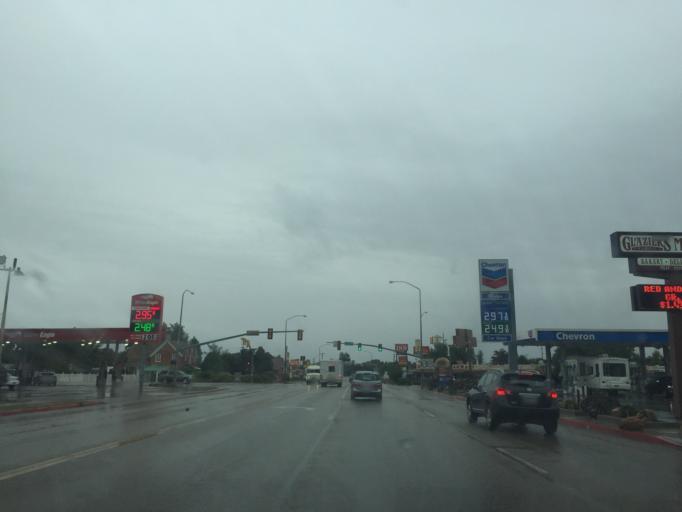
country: US
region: Utah
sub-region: Kane County
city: Kanab
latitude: 37.0438
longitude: -112.5264
